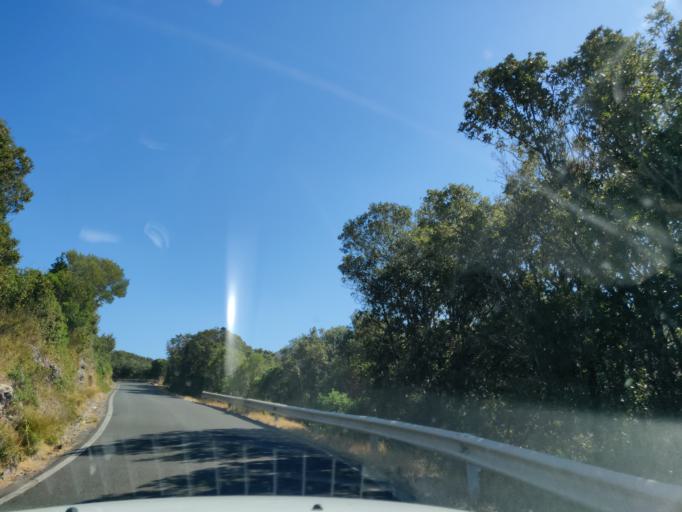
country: IT
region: Tuscany
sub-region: Provincia di Grosseto
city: Porto Ercole
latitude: 42.4304
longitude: 11.1706
